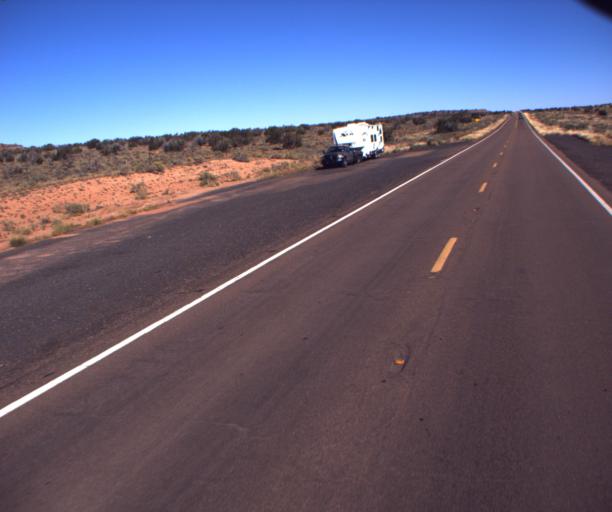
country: US
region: Arizona
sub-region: Navajo County
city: Snowflake
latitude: 34.6717
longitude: -110.1021
